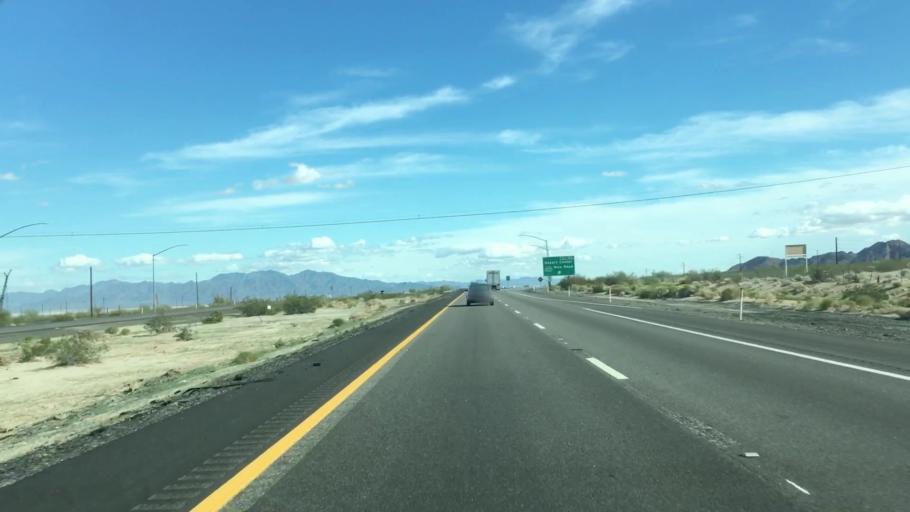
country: US
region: California
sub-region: Imperial County
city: Niland
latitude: 33.7103
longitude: -115.4056
